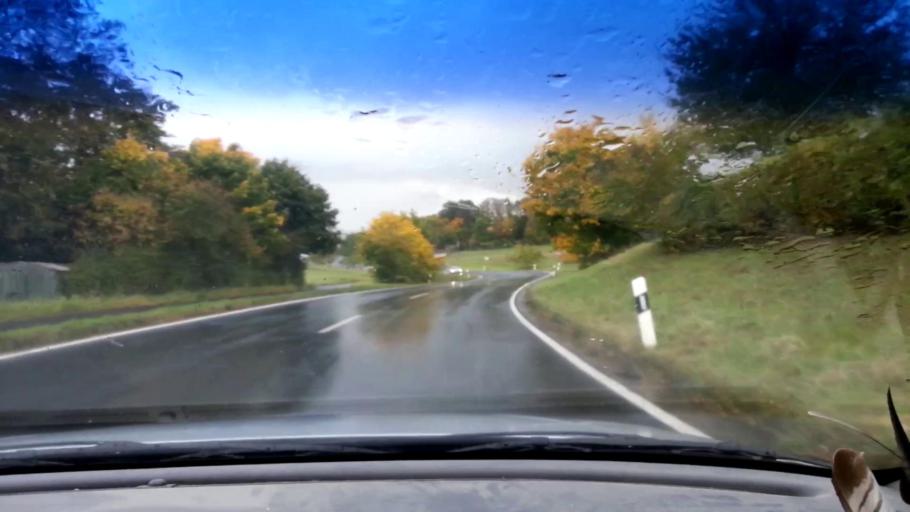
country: DE
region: Bavaria
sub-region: Upper Franconia
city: Burgebrach
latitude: 49.8438
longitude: 10.7313
